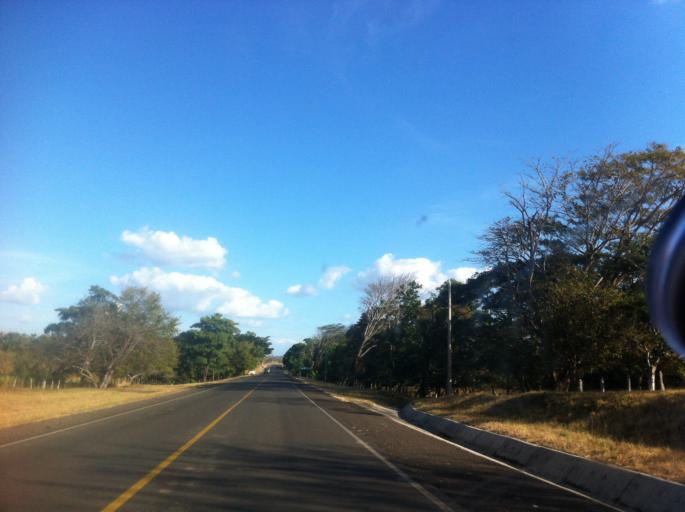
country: NI
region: Chontales
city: Acoyapa
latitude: 11.9254
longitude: -85.1374
